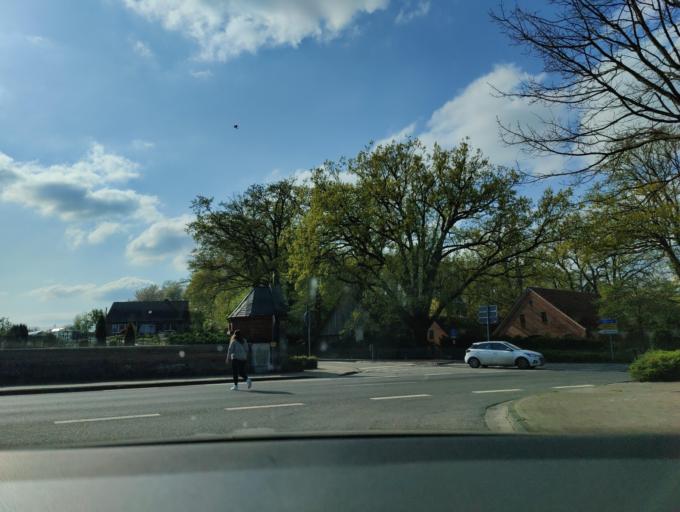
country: DE
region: Lower Saxony
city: Emsburen
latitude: 52.3872
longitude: 7.2912
